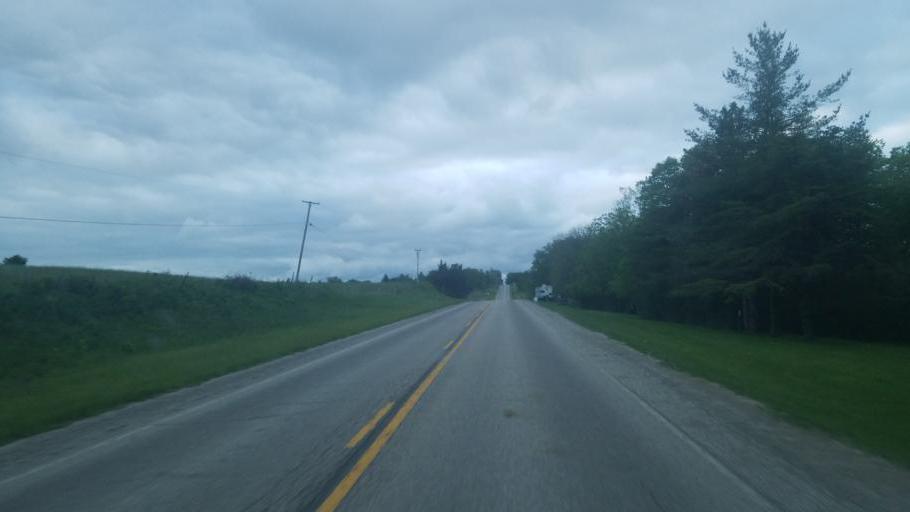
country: US
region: Iowa
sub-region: Decatur County
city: Lamoni
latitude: 40.6066
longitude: -93.9390
